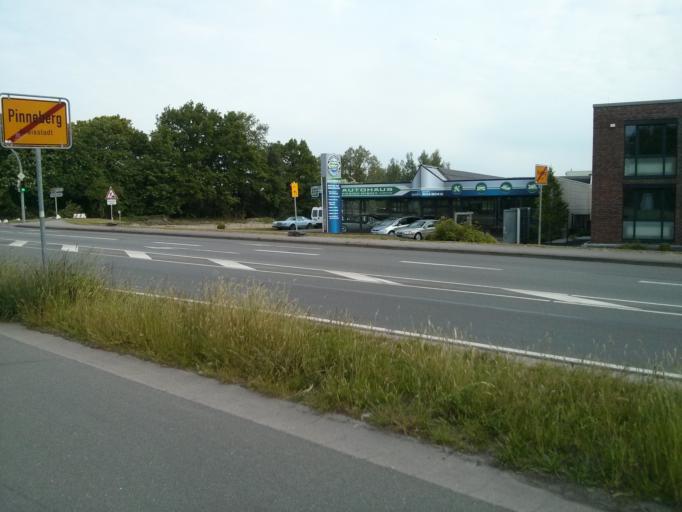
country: DE
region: Schleswig-Holstein
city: Pinneberg
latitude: 53.6579
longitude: 9.7750
